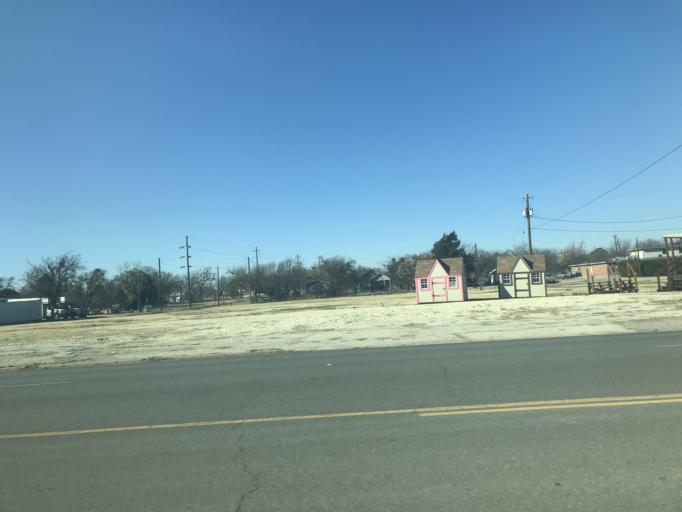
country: US
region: Texas
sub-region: Taylor County
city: Abilene
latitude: 32.4613
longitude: -99.7257
